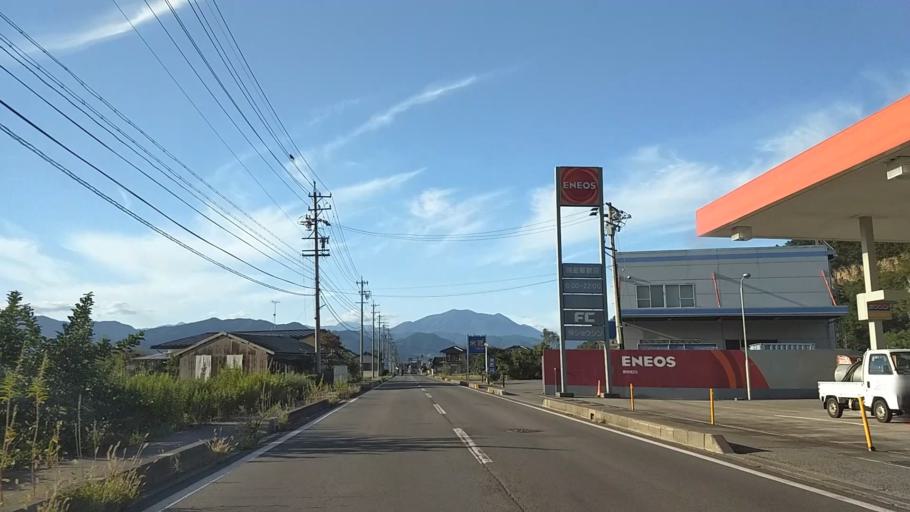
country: JP
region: Nagano
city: Nagano-shi
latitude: 36.5825
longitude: 138.2010
